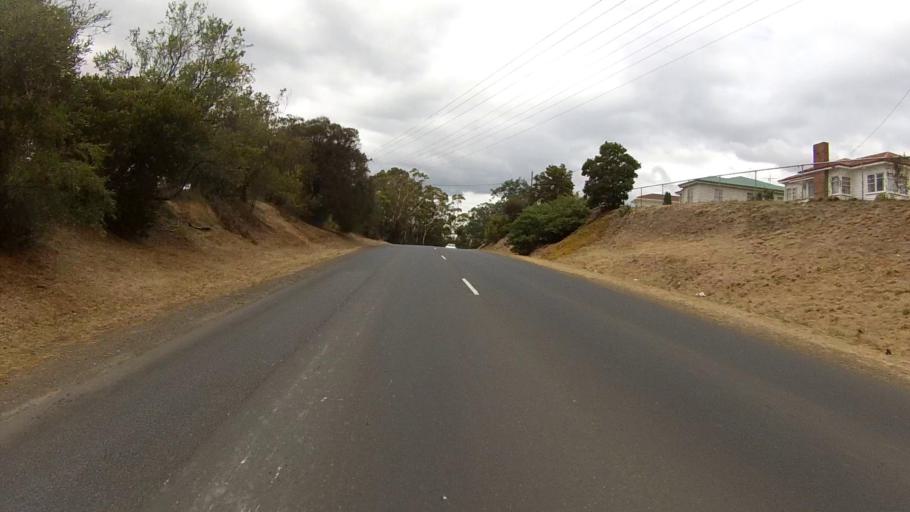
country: AU
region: Tasmania
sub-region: Glenorchy
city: Austins Ferry
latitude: -42.7735
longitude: 147.2490
